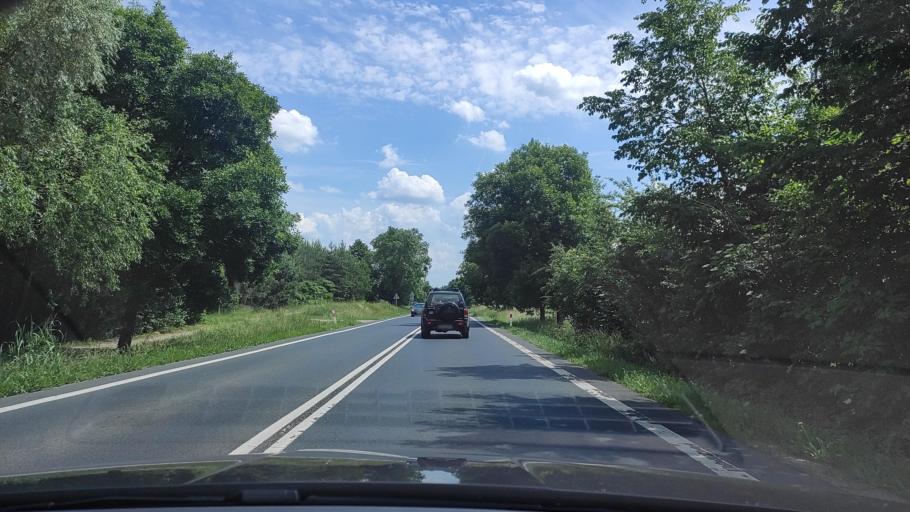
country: PL
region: Greater Poland Voivodeship
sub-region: Powiat gnieznienski
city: Lubowo
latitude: 52.5075
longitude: 17.3684
